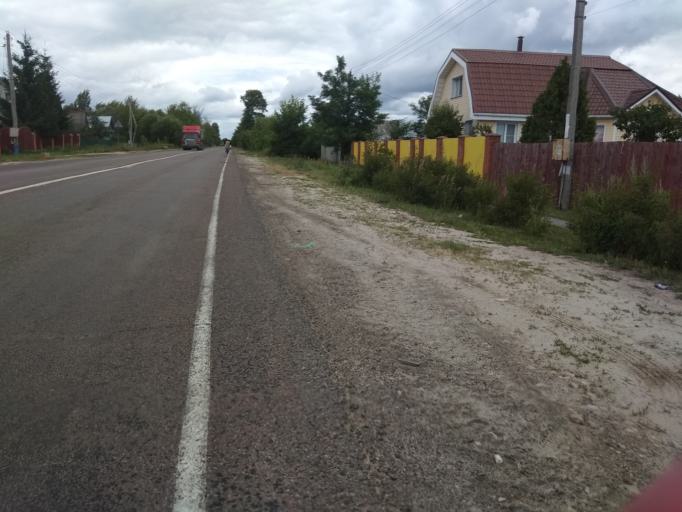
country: RU
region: Moskovskaya
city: Kerva
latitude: 55.5929
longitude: 39.7011
